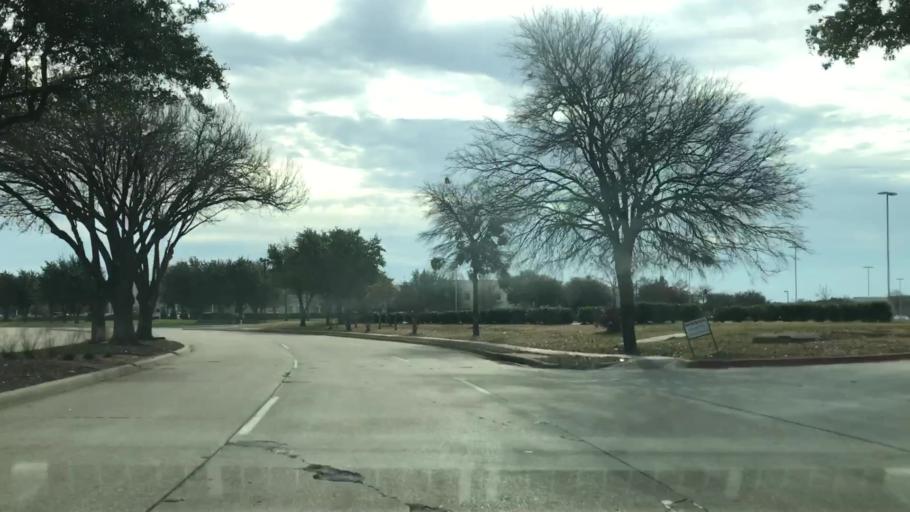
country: US
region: Texas
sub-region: Dallas County
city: Coppell
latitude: 32.9276
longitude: -97.0051
